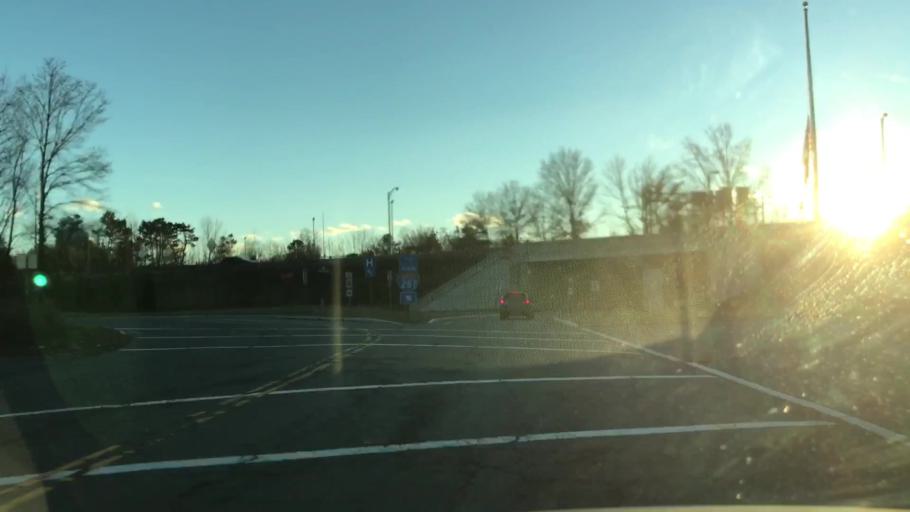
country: US
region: New Jersey
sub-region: Morris County
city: Parsippany
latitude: 40.8674
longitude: -74.4159
